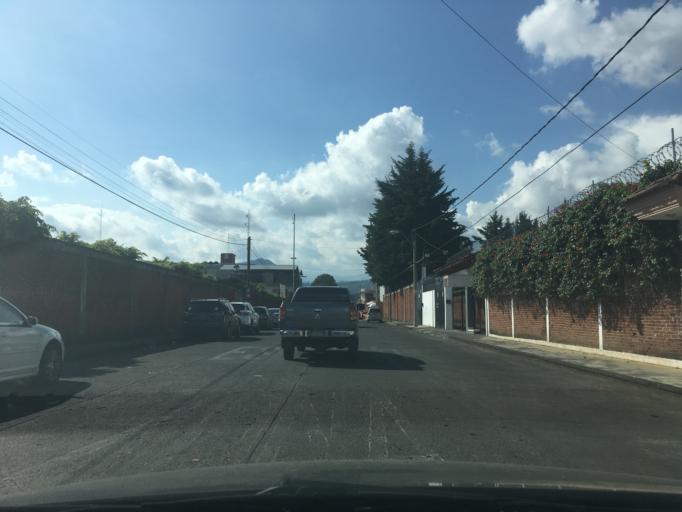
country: MX
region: Michoacan
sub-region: Uruapan
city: Uruapan
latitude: 19.4081
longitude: -102.0548
